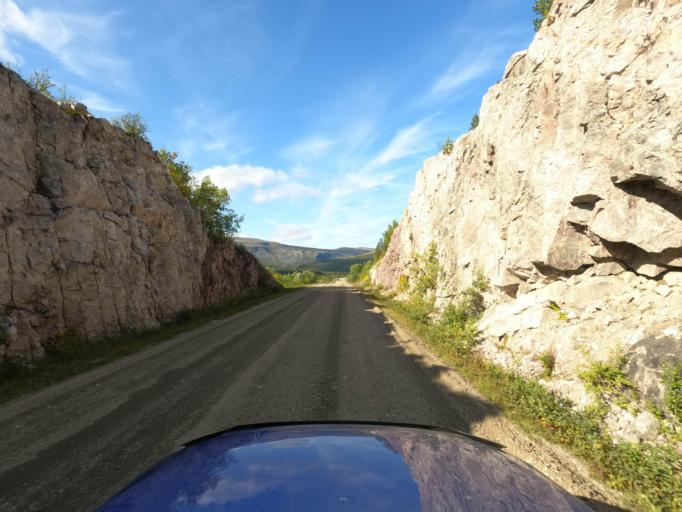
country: NO
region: Finnmark Fylke
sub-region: Porsanger
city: Lakselv
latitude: 69.8904
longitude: 25.0022
